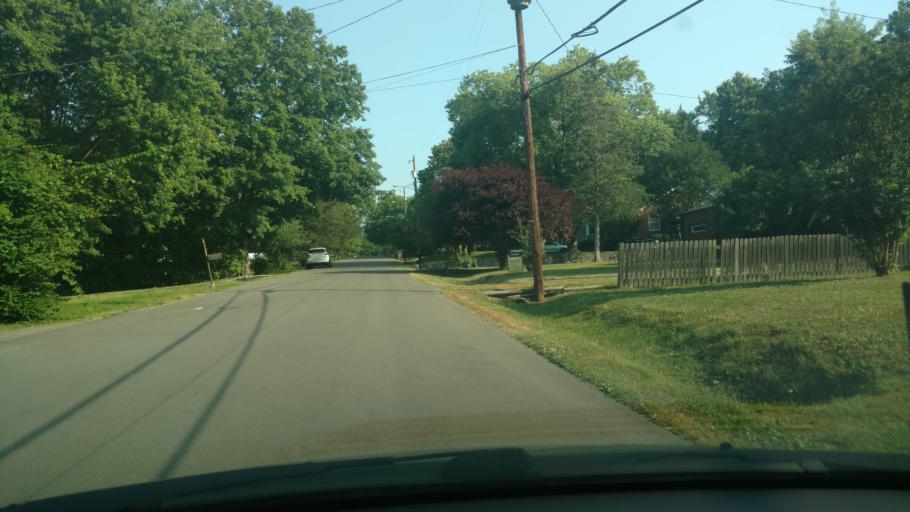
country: US
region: Tennessee
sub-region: Davidson County
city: Lakewood
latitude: 36.2117
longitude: -86.7135
